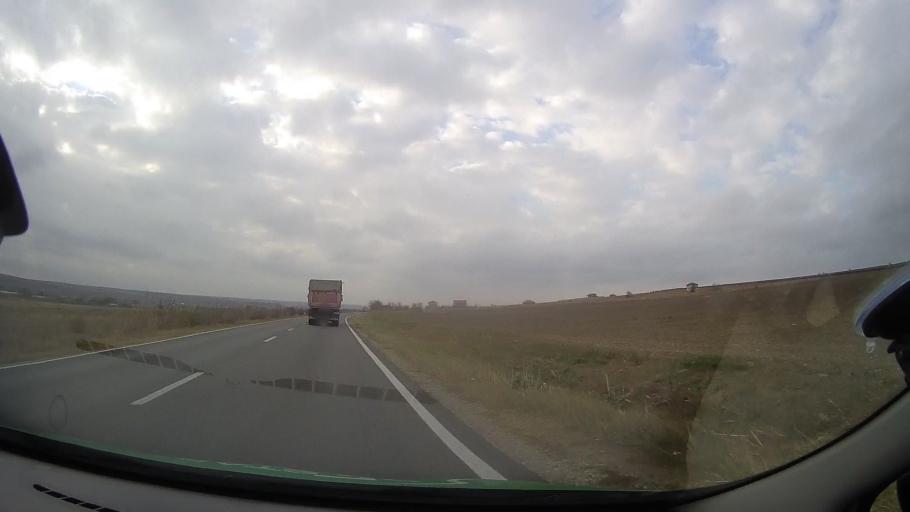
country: RO
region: Constanta
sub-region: Comuna Mircea Voda
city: Satu Nou
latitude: 44.2654
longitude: 28.2444
